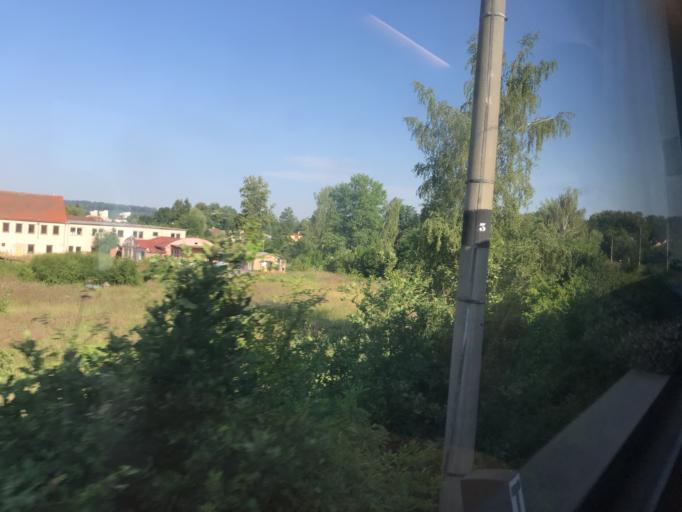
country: CZ
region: Jihocesky
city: Sobeslav
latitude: 49.2604
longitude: 14.7262
